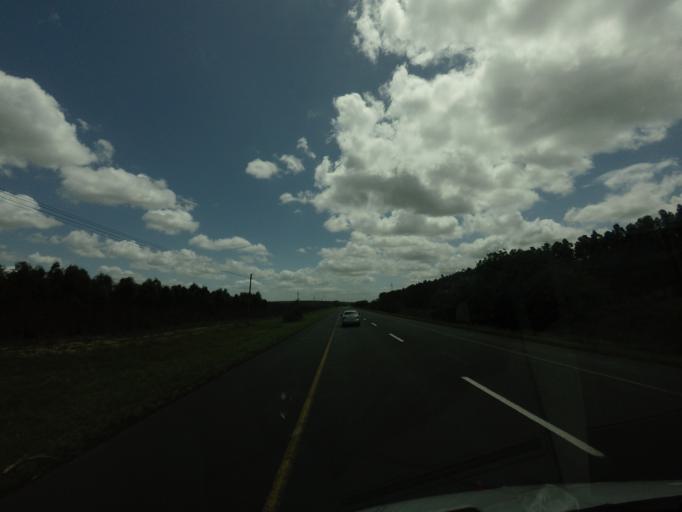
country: ZA
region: KwaZulu-Natal
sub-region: uThungulu District Municipality
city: KwaMbonambi
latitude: -28.5568
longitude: 32.1172
